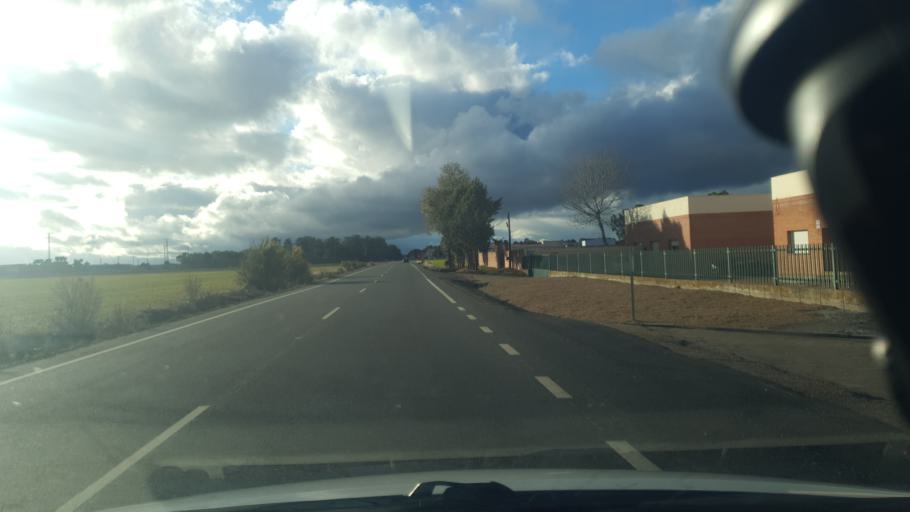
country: ES
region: Castille and Leon
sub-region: Provincia de Segovia
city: Nava de la Asuncion
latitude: 41.1559
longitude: -4.5032
